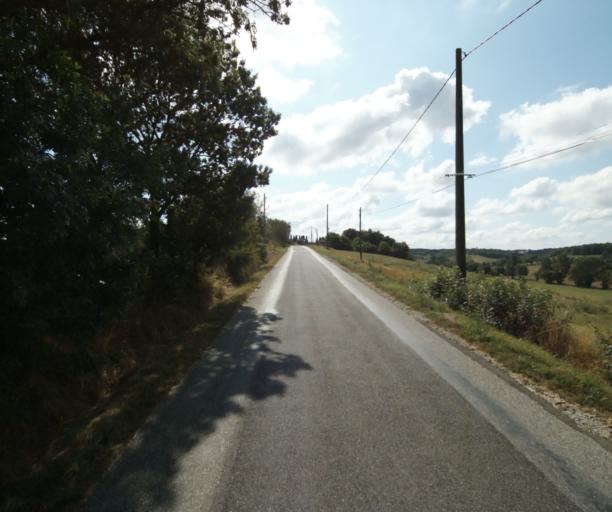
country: FR
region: Midi-Pyrenees
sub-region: Departement de la Haute-Garonne
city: Saint-Felix-Lauragais
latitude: 43.4445
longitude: 1.8151
